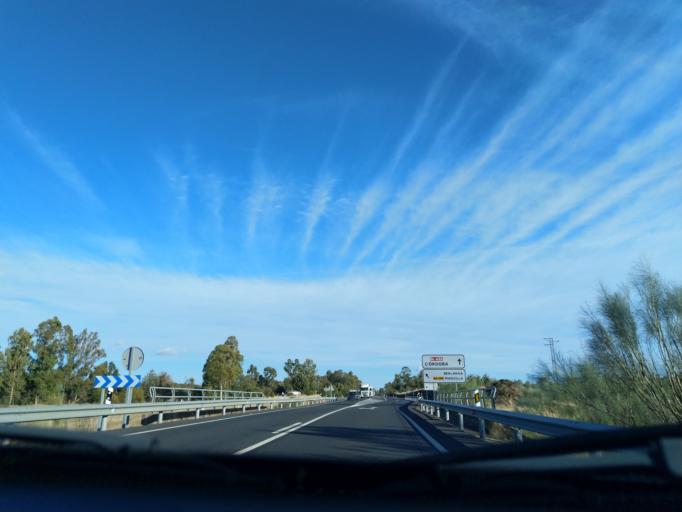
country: ES
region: Extremadura
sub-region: Provincia de Badajoz
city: Berlanga
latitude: 38.2755
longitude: -5.8224
